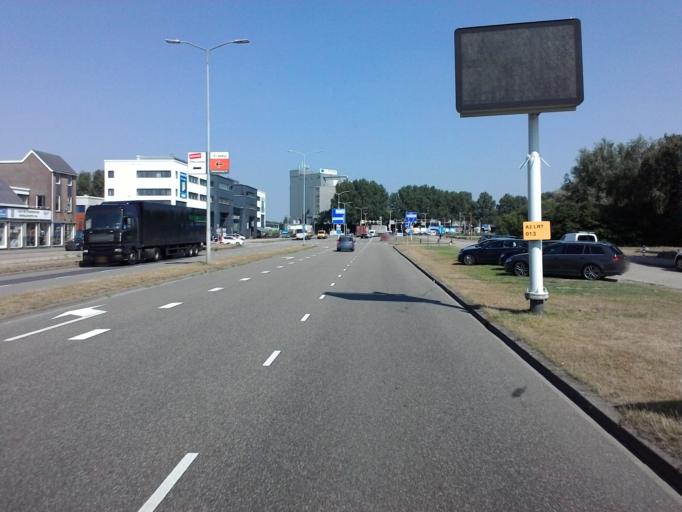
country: NL
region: Utrecht
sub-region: Stichtse Vecht
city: Maarssen
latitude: 52.1160
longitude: 5.0529
